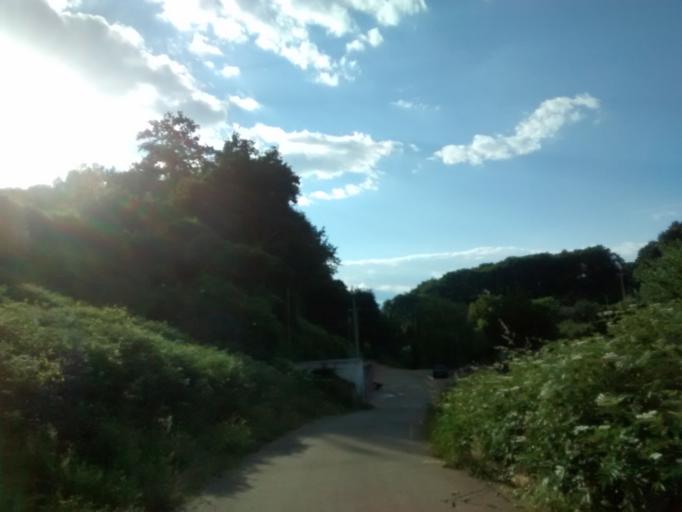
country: IT
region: Calabria
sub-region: Provincia di Catanzaro
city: Cortale
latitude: 38.8836
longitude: 16.4091
